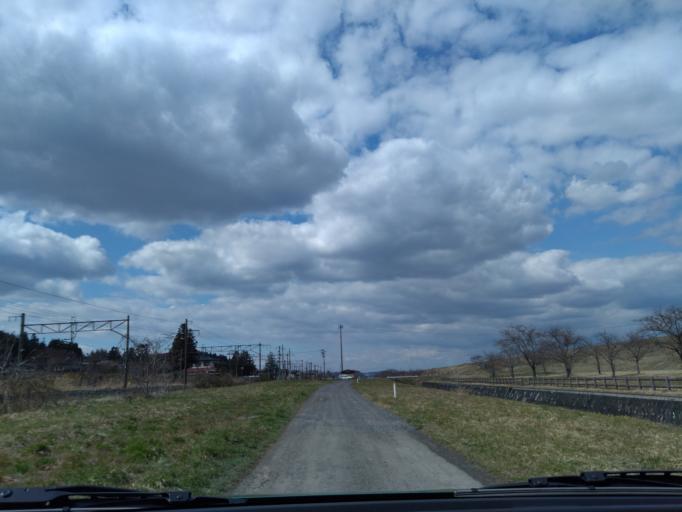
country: JP
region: Iwate
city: Ichinoseki
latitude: 38.9522
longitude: 141.1320
